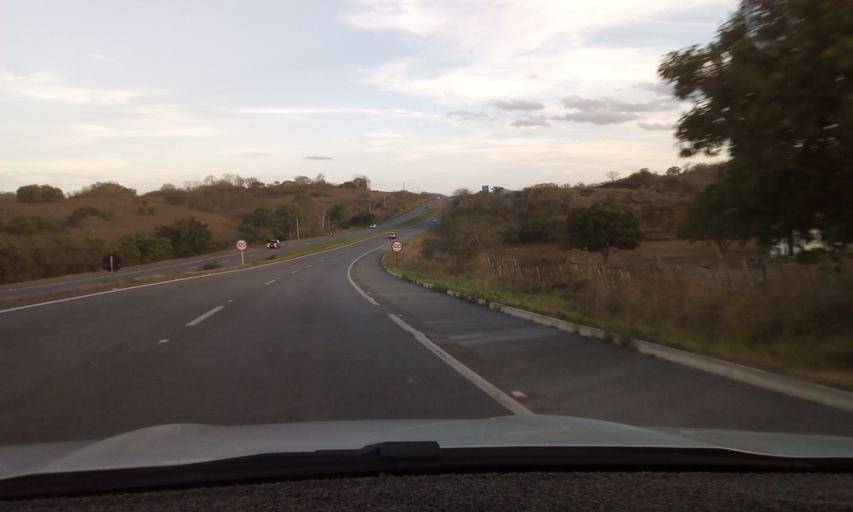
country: BR
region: Paraiba
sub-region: Massaranduba
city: Massaranduba
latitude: -7.2623
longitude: -35.8046
